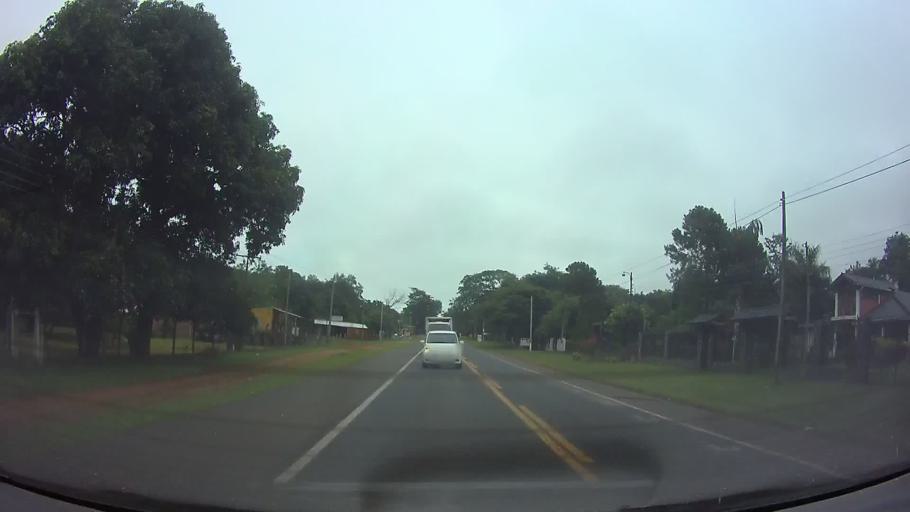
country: PY
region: Paraguari
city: Paraguari
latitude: -25.5993
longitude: -57.2014
